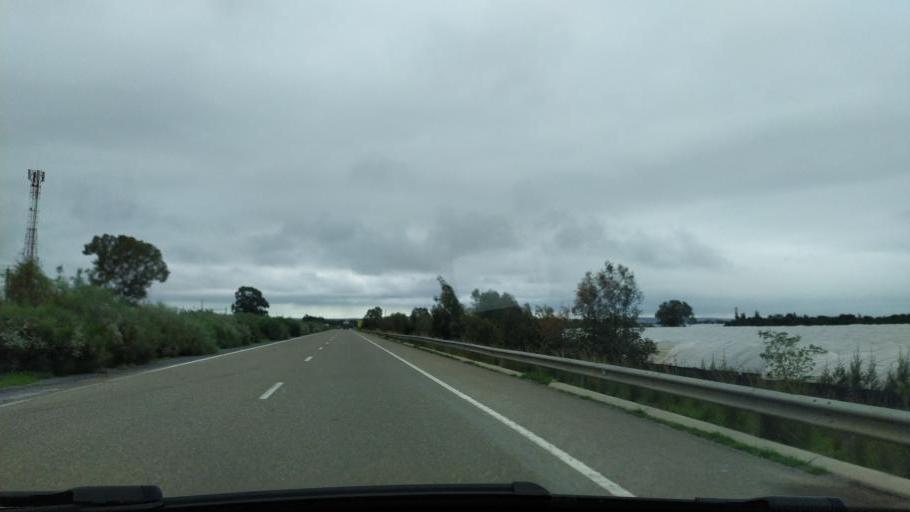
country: MA
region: Gharb-Chrarda-Beni Hssen
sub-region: Kenitra Province
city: Lalla Mimouna
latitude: 34.8908
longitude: -6.2101
